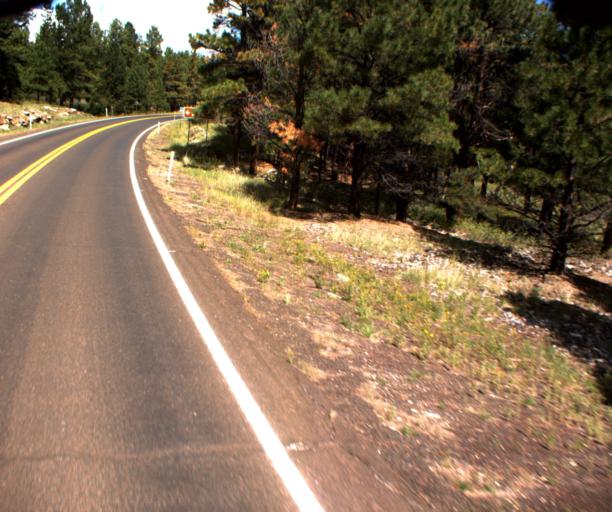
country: US
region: Arizona
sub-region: Apache County
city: Eagar
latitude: 34.0405
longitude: -109.4579
